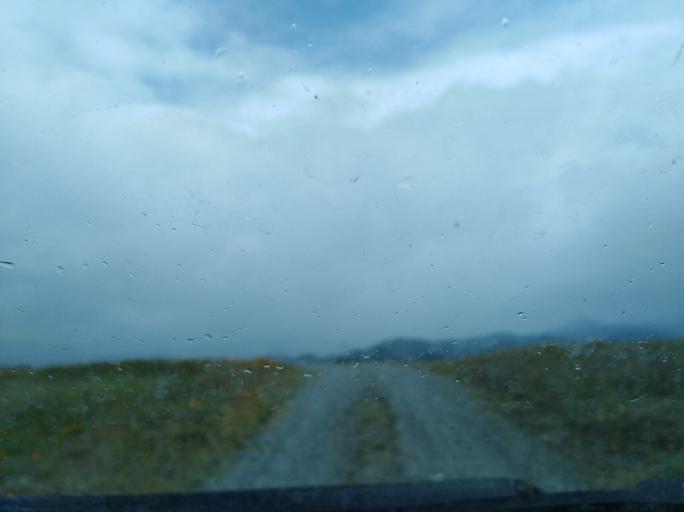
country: NZ
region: Marlborough
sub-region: Marlborough District
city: Blenheim
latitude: -41.4406
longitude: 174.0111
